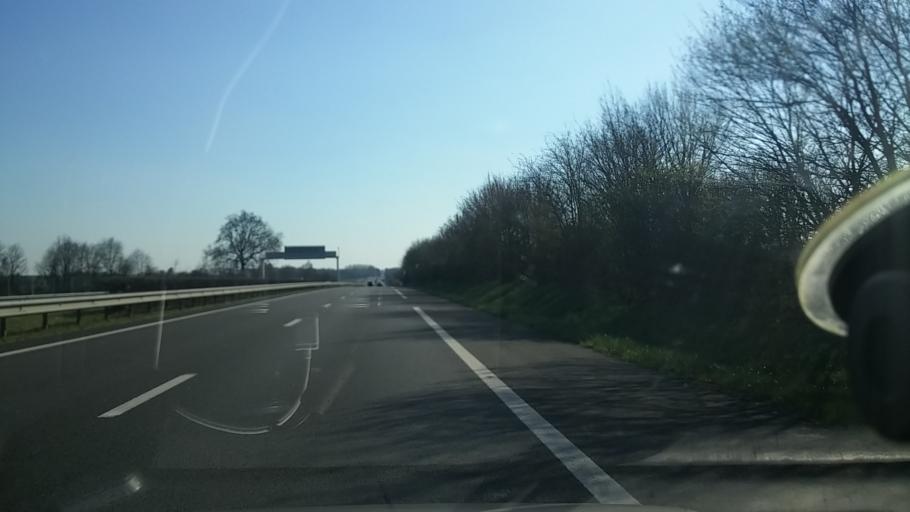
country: FR
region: Centre
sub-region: Departement du Cher
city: Massay
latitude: 47.1875
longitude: 2.0165
